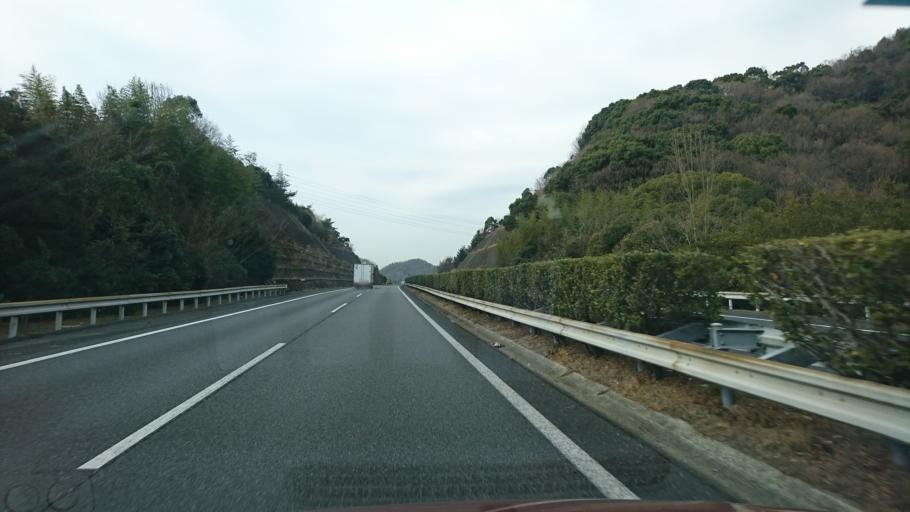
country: JP
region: Okayama
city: Kasaoka
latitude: 34.5320
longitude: 133.5415
